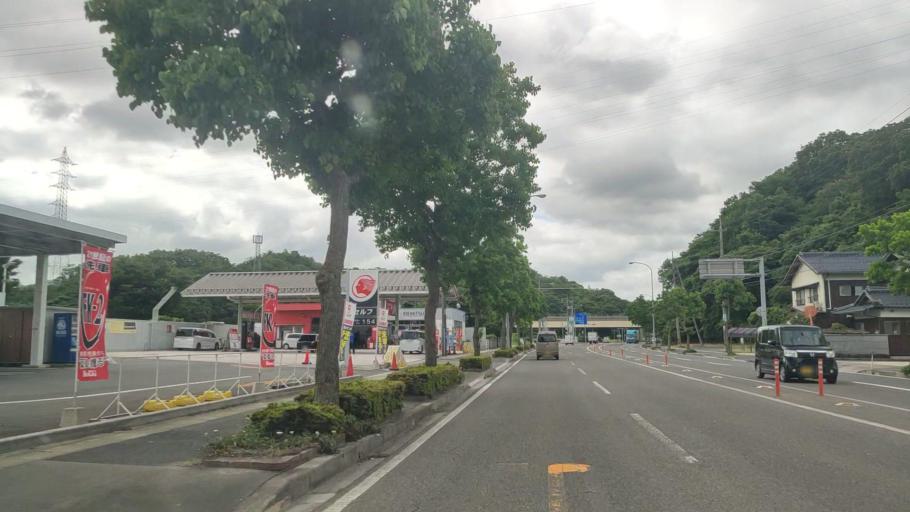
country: JP
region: Tottori
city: Yonago
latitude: 35.4185
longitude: 133.3518
